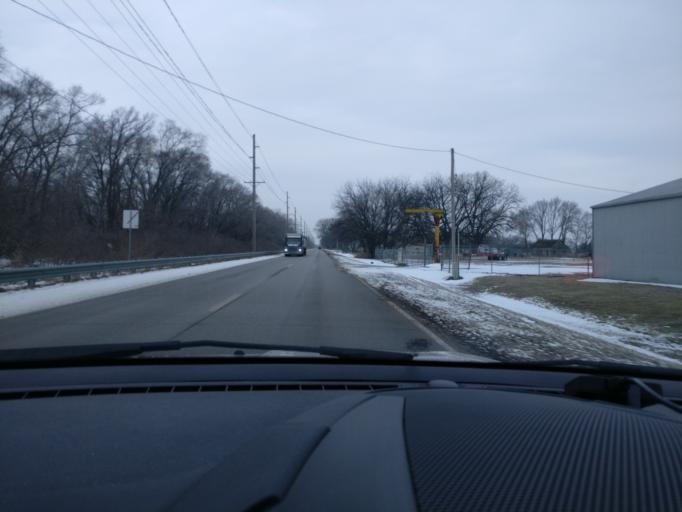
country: US
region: Nebraska
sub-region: Dodge County
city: Fremont
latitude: 41.4392
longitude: -96.5256
